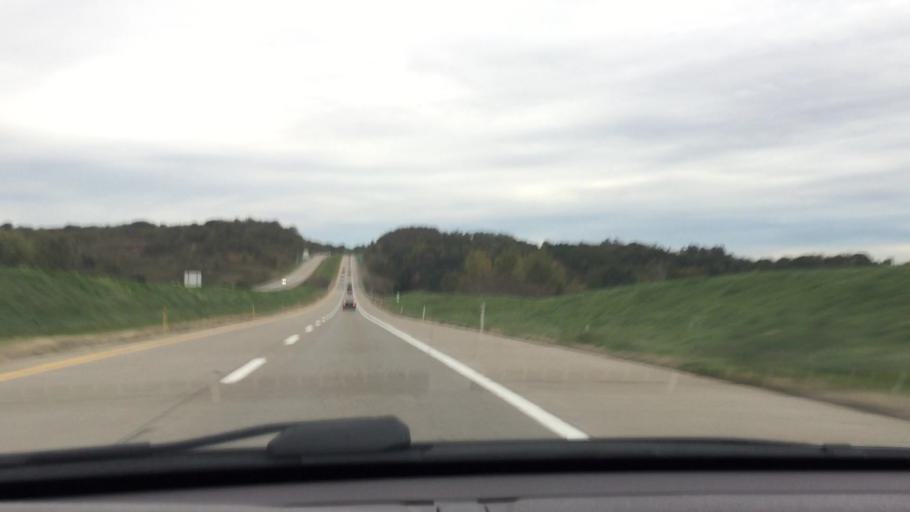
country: US
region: Pennsylvania
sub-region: Lawrence County
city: Oakland
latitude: 40.9538
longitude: -80.3934
